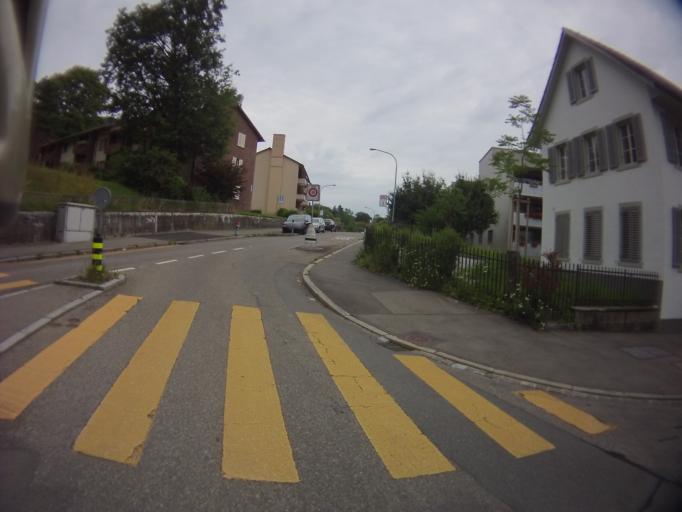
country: CH
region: Zurich
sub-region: Bezirk Zuerich
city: Zuerich (Kreis 2) / Mittel-Leimbach
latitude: 47.3286
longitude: 8.5129
